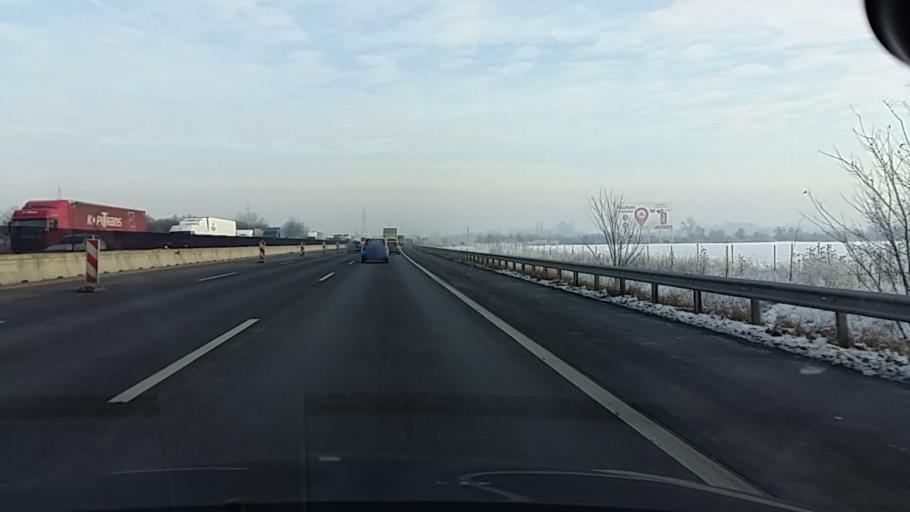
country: HU
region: Pest
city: Dunaharaszti
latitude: 47.3760
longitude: 19.0780
